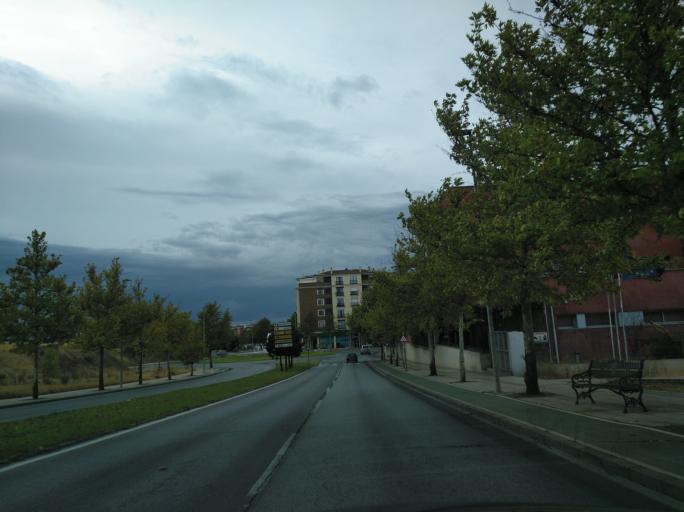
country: ES
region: Extremadura
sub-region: Provincia de Badajoz
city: Badajoz
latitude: 38.8637
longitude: -6.9756
